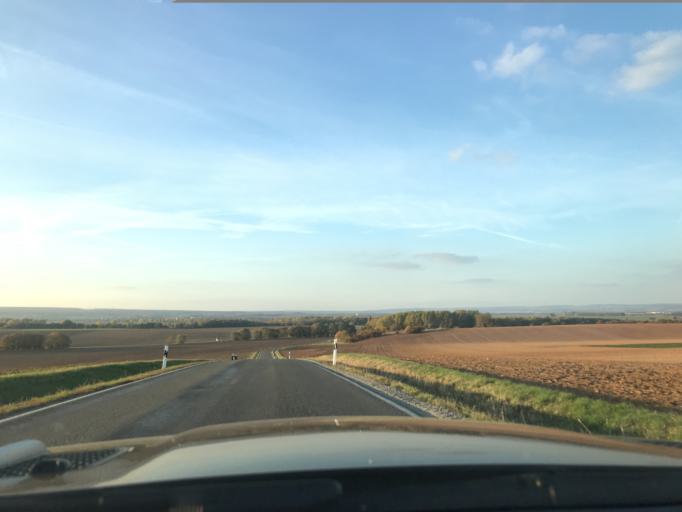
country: DE
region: Thuringia
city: Flarchheim
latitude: 51.1326
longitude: 10.4721
